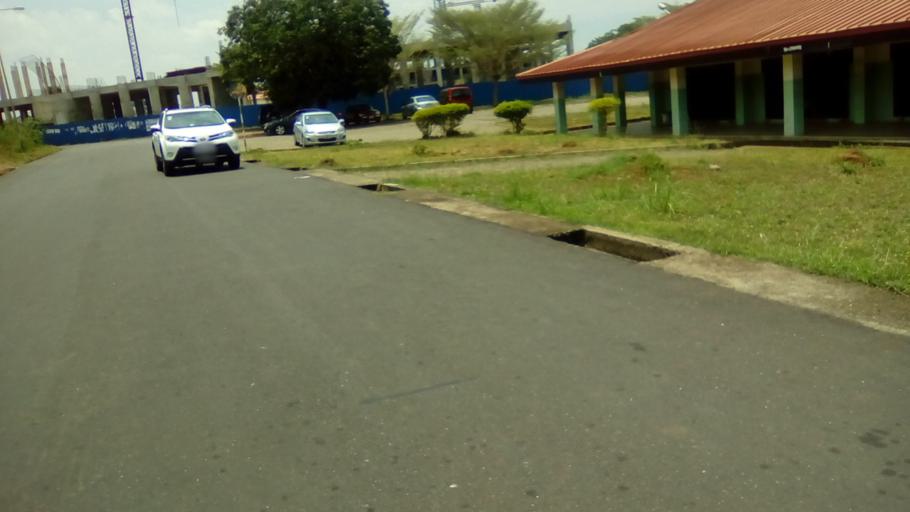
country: GH
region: Greater Accra
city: Medina Estates
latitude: 5.6557
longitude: -0.1881
